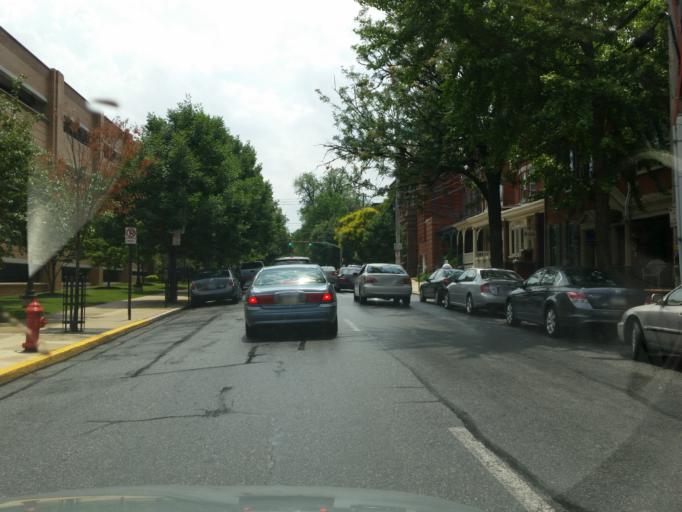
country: US
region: Pennsylvania
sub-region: Lancaster County
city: Lancaster
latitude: 40.0469
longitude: -76.3053
